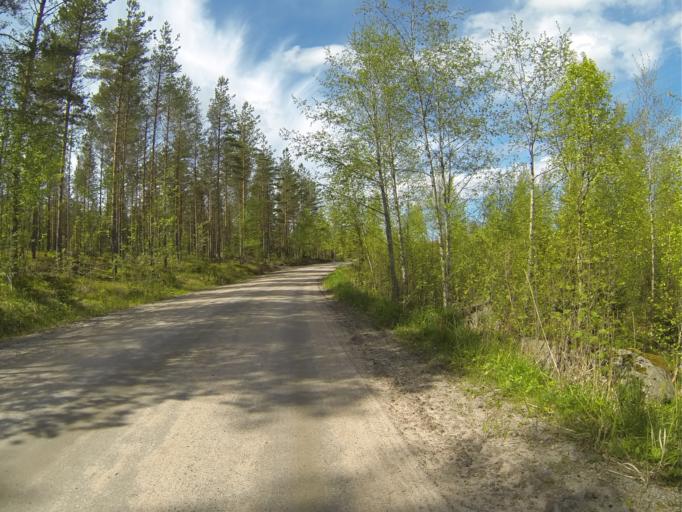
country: FI
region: Varsinais-Suomi
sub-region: Salo
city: Halikko
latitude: 60.3248
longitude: 23.0655
